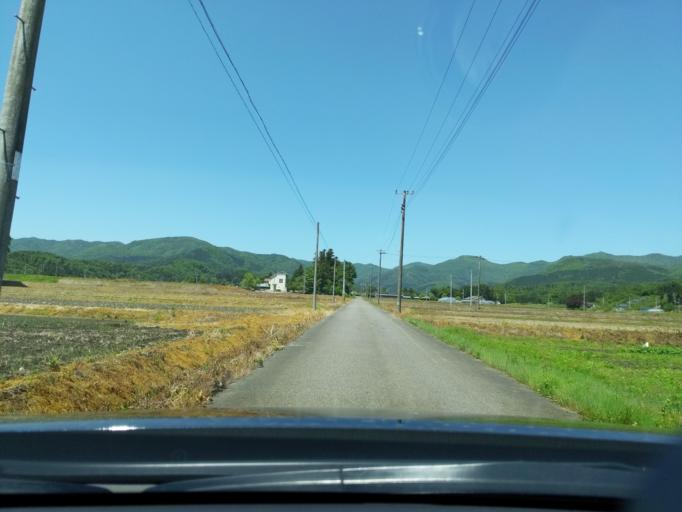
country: JP
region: Fukushima
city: Koriyama
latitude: 37.4049
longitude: 140.2658
